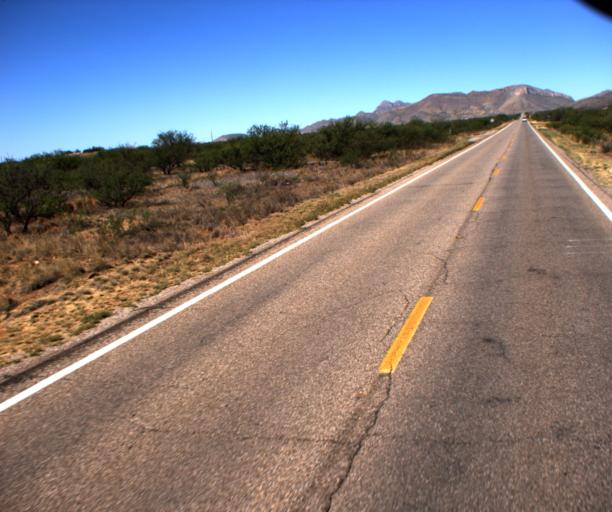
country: US
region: Arizona
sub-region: Cochise County
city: Huachuca City
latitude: 31.6925
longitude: -110.3614
